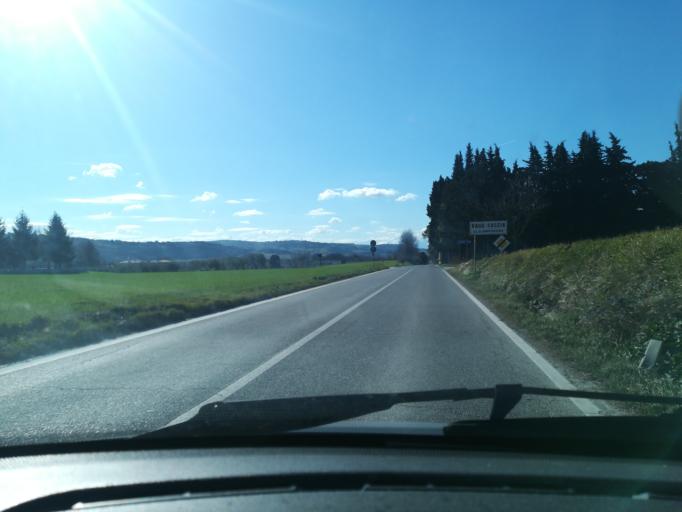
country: IT
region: The Marches
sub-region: Provincia di Macerata
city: Montecassiano
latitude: 43.3511
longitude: 13.4364
